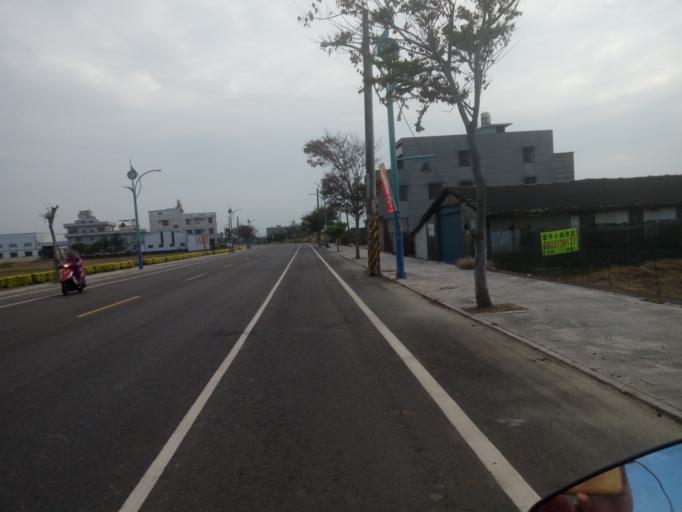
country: TW
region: Taiwan
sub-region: Chiayi
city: Taibao
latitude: 23.4814
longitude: 120.3350
